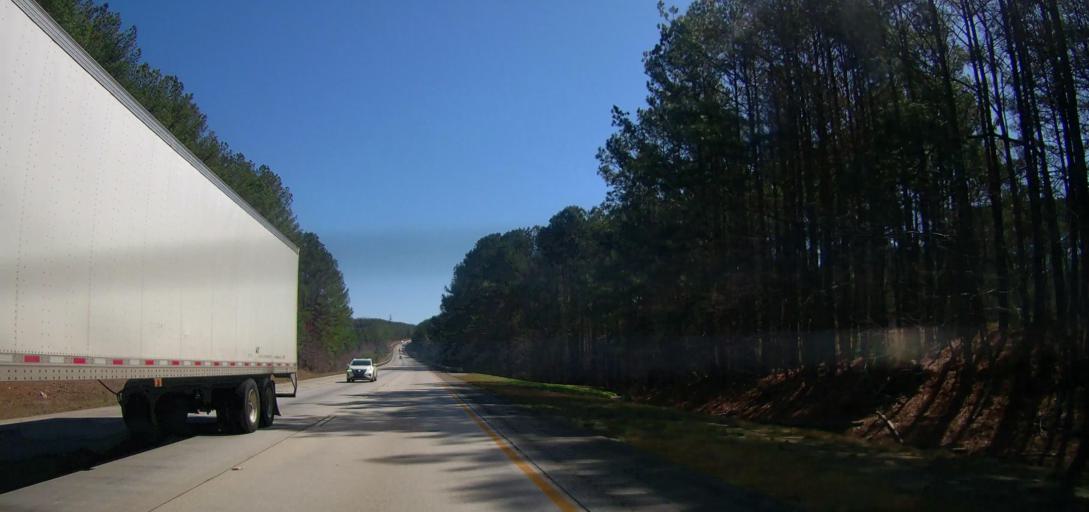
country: US
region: Georgia
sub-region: Haralson County
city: Tallapoosa
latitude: 33.6861
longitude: -85.2564
